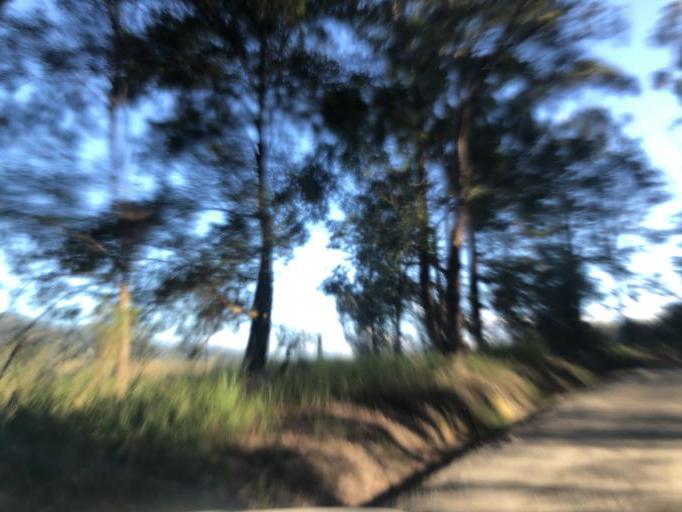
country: AU
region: New South Wales
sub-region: Nambucca Shire
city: Nambucca
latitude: -30.5842
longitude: 152.9371
